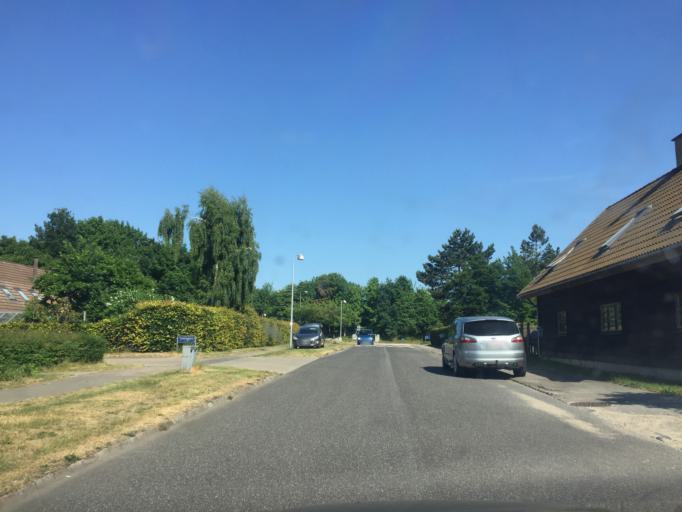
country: DK
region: Capital Region
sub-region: Ballerup Kommune
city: Malov
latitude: 55.7846
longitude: 12.3260
